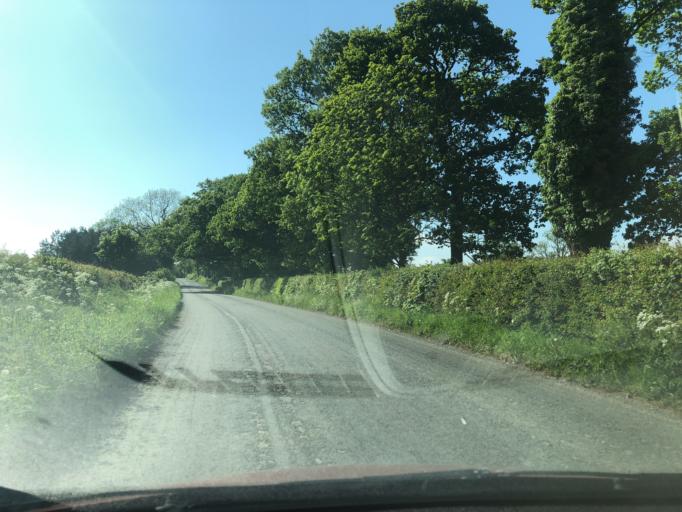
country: GB
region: England
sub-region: North Yorkshire
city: Northallerton
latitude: 54.3207
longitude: -1.3830
